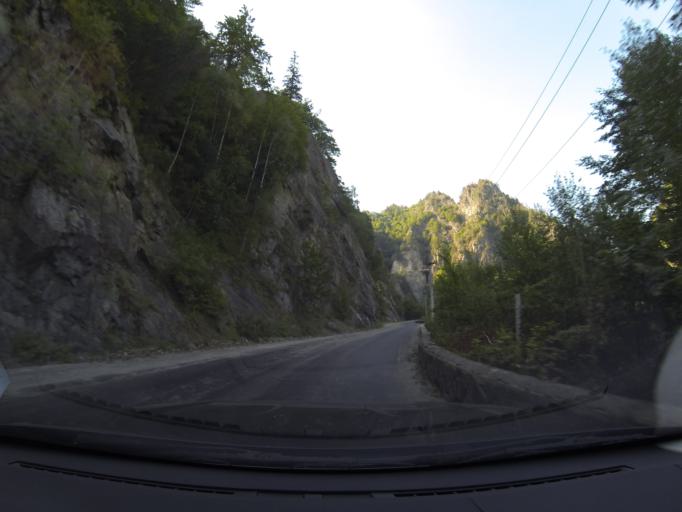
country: RO
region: Arges
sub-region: Comuna Arefu
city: Arefu
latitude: 45.3552
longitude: 24.6272
